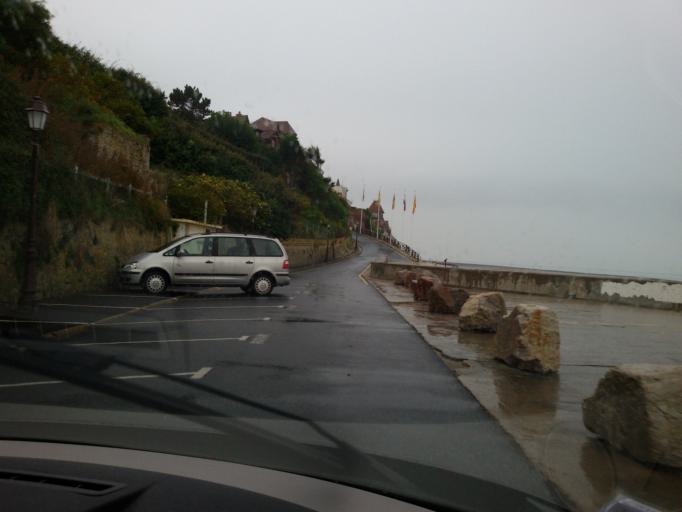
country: FR
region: Lower Normandy
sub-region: Departement du Calvados
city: Trouville-sur-Mer
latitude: 49.4029
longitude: 0.1297
